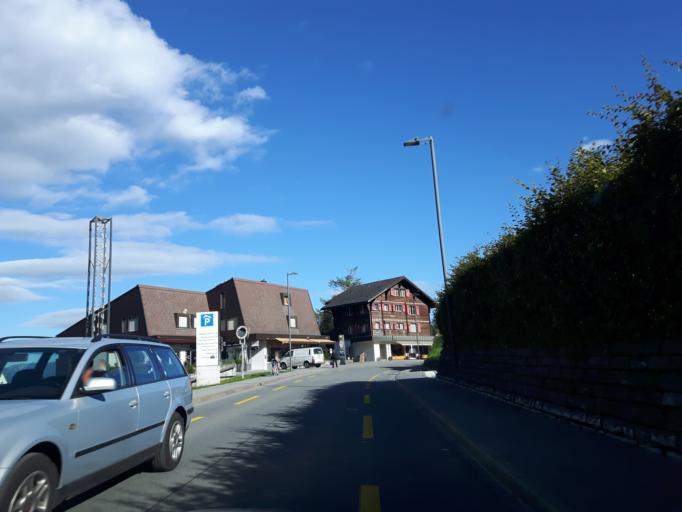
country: CH
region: Grisons
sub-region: Imboden District
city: Flims
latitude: 46.8292
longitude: 9.2871
